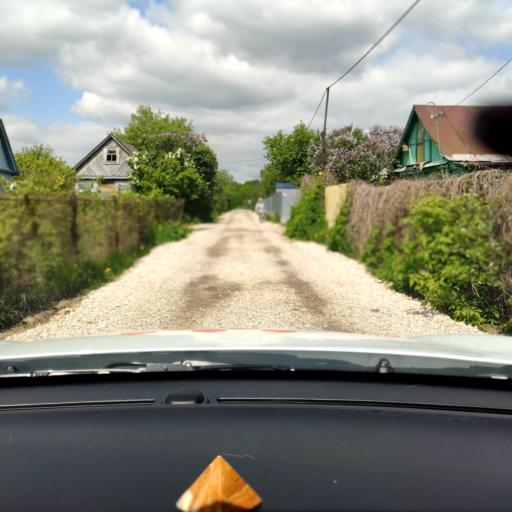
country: RU
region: Tatarstan
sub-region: Gorod Kazan'
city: Kazan
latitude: 55.8621
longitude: 49.1839
